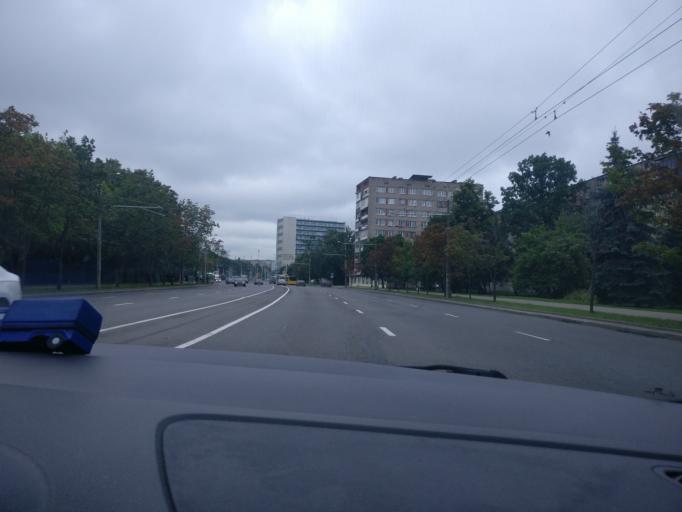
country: BY
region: Minsk
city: Minsk
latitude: 53.8814
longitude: 27.6120
